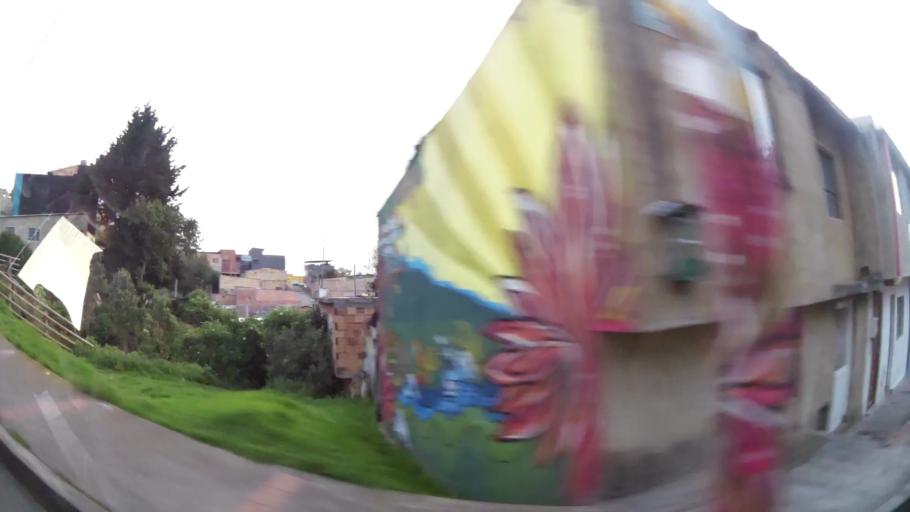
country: CO
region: Bogota D.C.
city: Bogota
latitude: 4.5431
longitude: -74.0819
